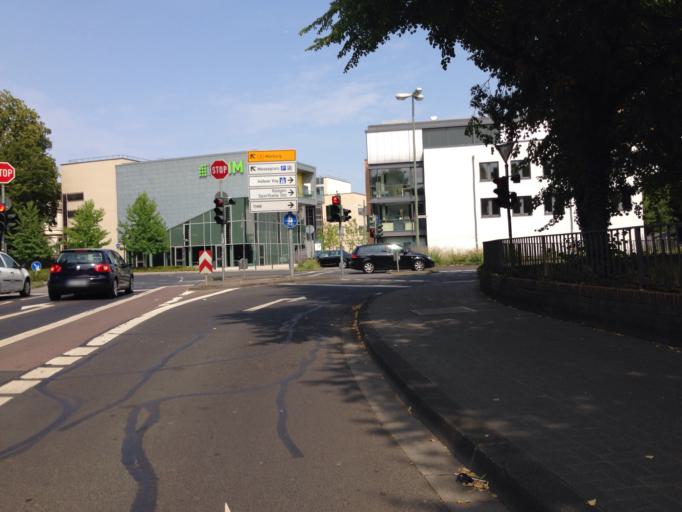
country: DE
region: Hesse
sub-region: Regierungsbezirk Giessen
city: Giessen
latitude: 50.5863
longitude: 8.6810
